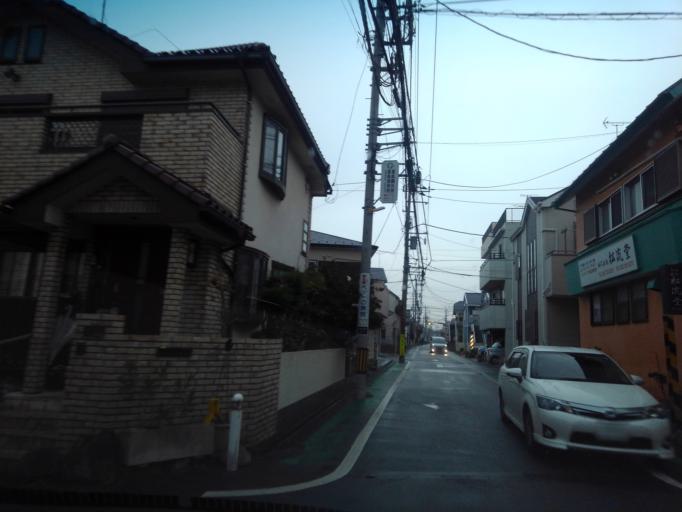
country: JP
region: Tokyo
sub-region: Machida-shi
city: Machida
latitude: 35.5135
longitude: 139.4418
